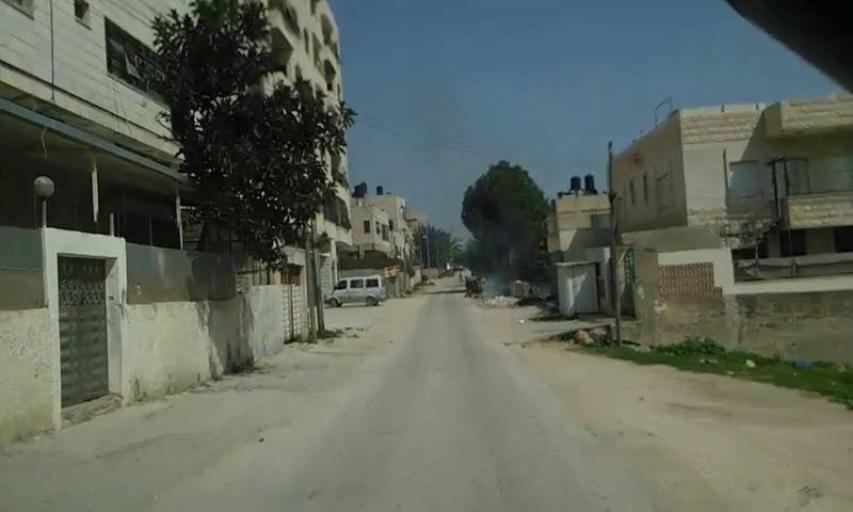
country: PS
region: West Bank
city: `Azmut
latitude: 32.2235
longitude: 35.2968
